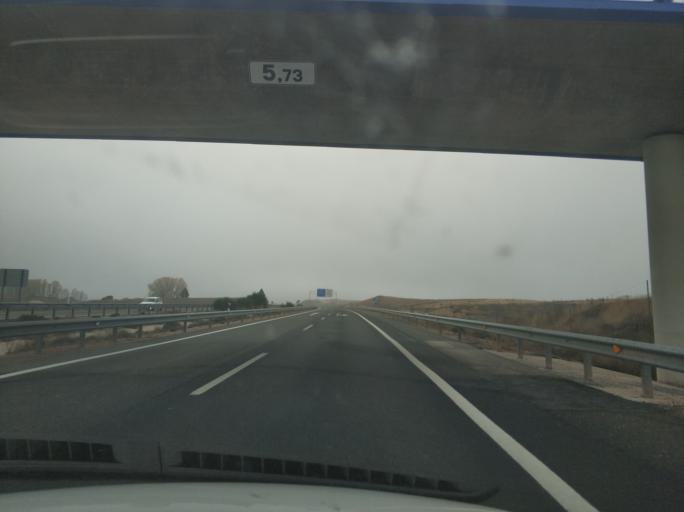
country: ES
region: Castille and Leon
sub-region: Provincia de Soria
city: Adradas
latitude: 41.3563
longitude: -2.4764
